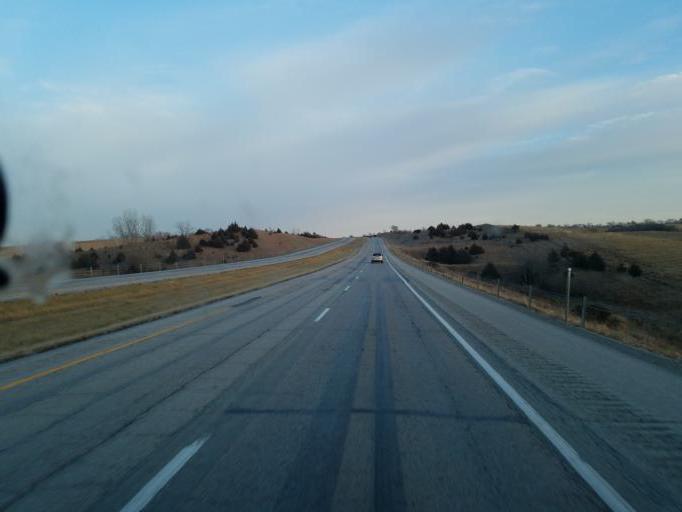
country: US
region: Iowa
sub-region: Harrison County
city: Missouri Valley
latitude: 41.4932
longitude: -95.8270
